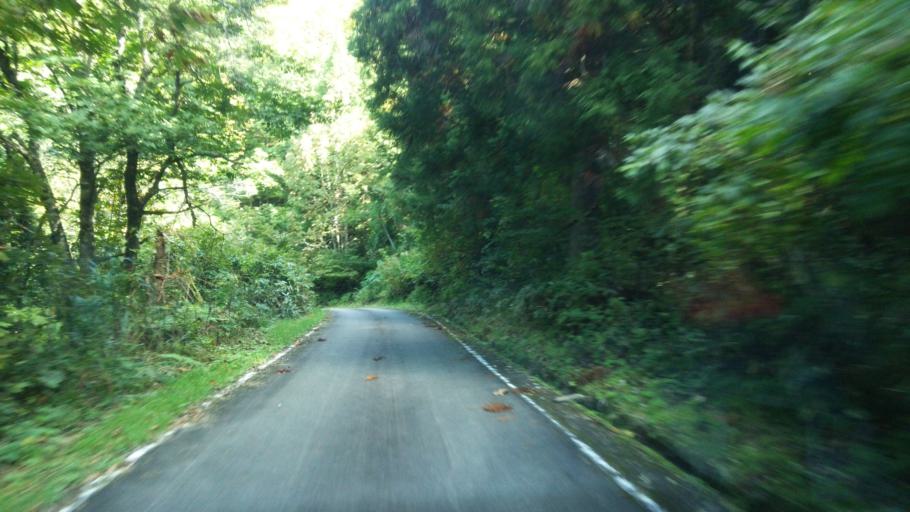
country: JP
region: Fukushima
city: Kitakata
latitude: 37.6117
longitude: 139.9876
